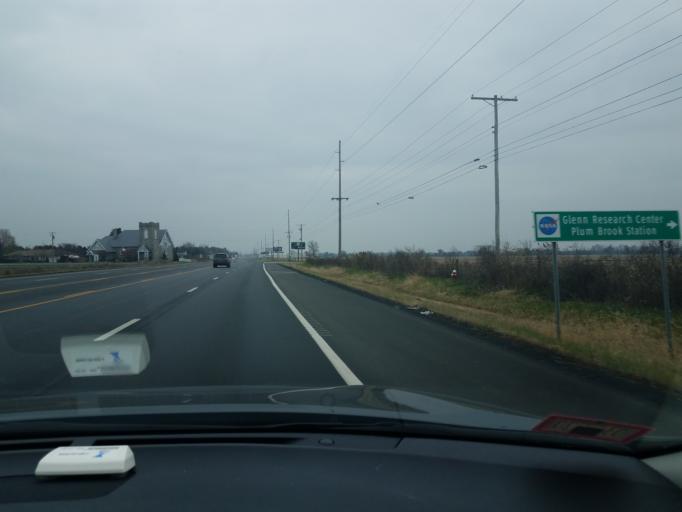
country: US
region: Ohio
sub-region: Erie County
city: Milan
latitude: 41.3604
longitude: -82.6366
